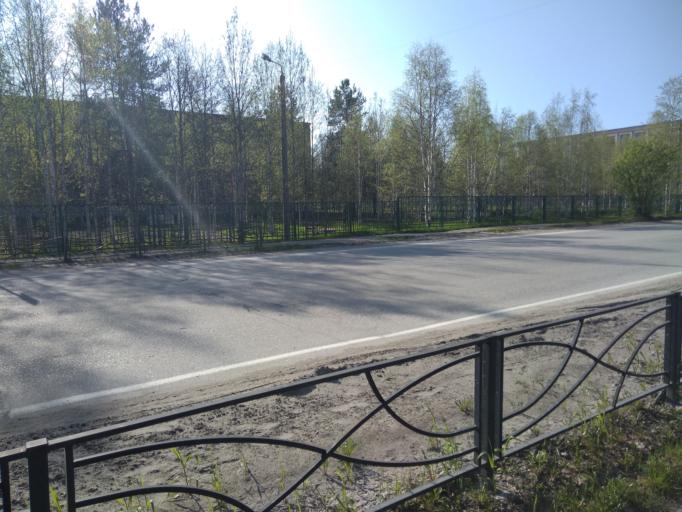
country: RU
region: Komi Republic
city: Pechora
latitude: 65.1217
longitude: 57.1542
